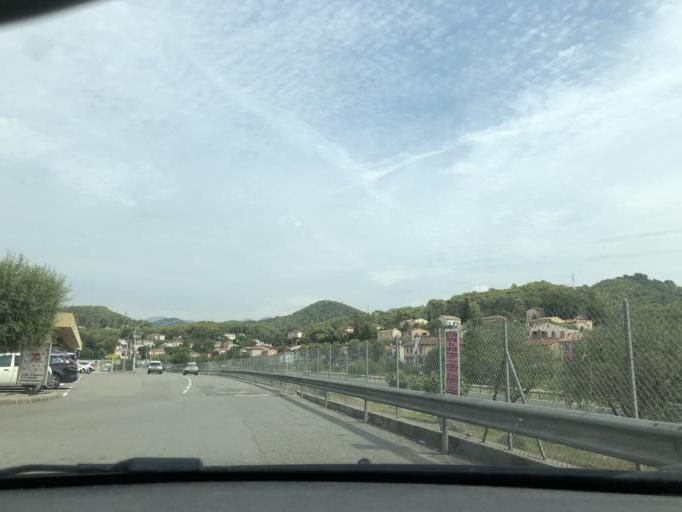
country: FR
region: Provence-Alpes-Cote d'Azur
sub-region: Departement des Alpes-Maritimes
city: Cantaron
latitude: 43.7775
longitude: 7.3369
